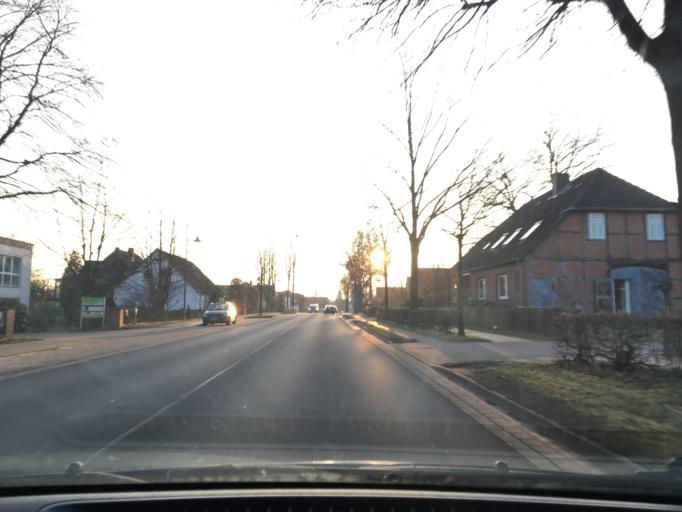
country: DE
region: Lower Saxony
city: Eschede
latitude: 52.7304
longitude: 10.2305
